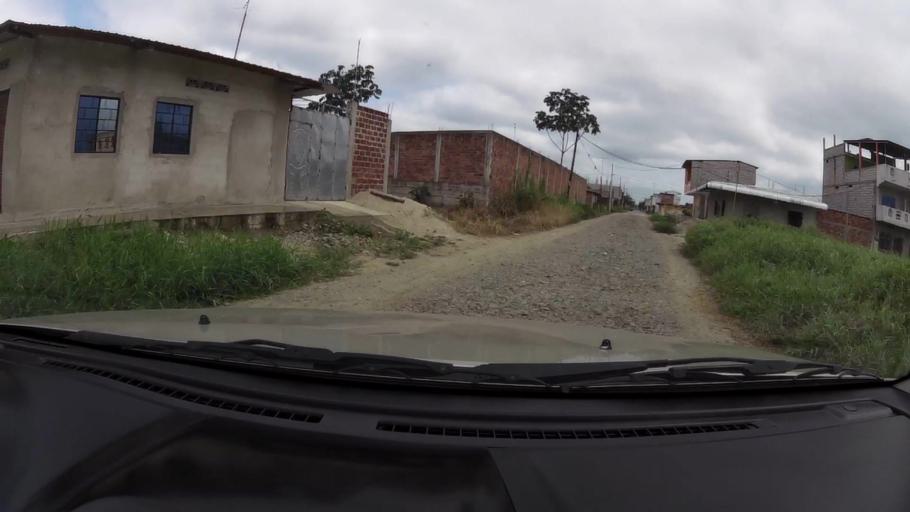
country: EC
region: Guayas
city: Naranjal
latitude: -2.6827
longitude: -79.6202
